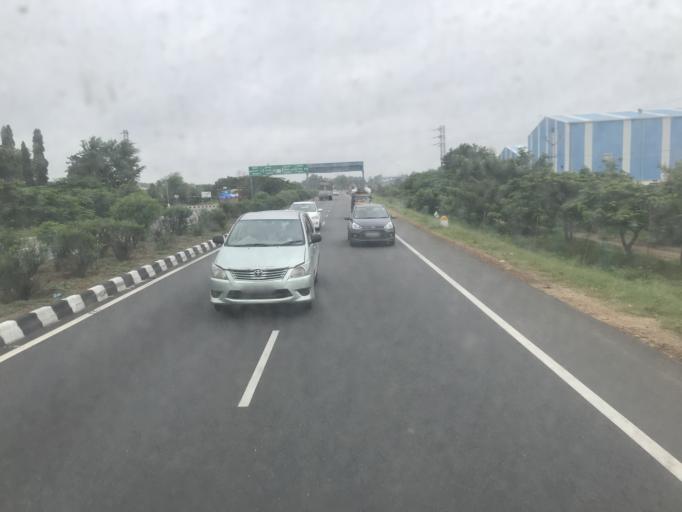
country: IN
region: Telangana
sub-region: Mahbubnagar
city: Farrukhnagar
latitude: 17.0260
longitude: 78.1982
